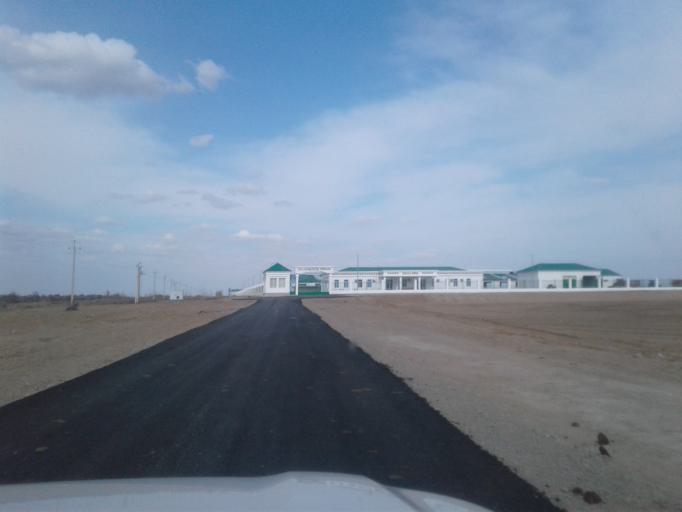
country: TM
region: Ahal
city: Ashgabat
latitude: 38.1945
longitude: 58.4195
